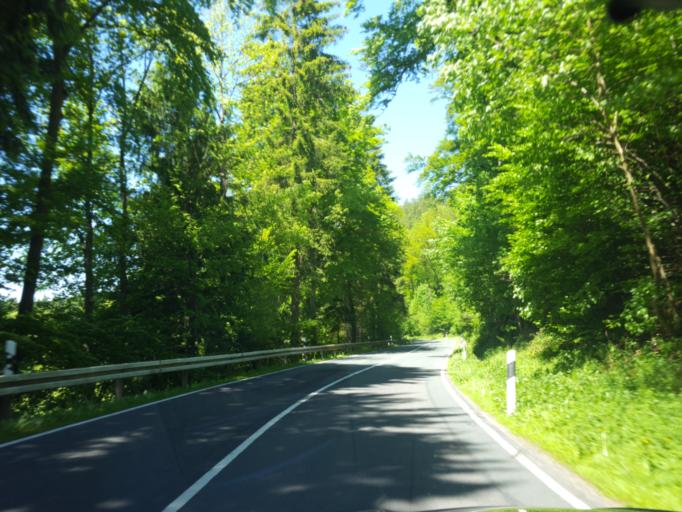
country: DE
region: North Rhine-Westphalia
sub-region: Regierungsbezirk Arnsberg
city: Olsberg
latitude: 51.3312
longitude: 8.4484
